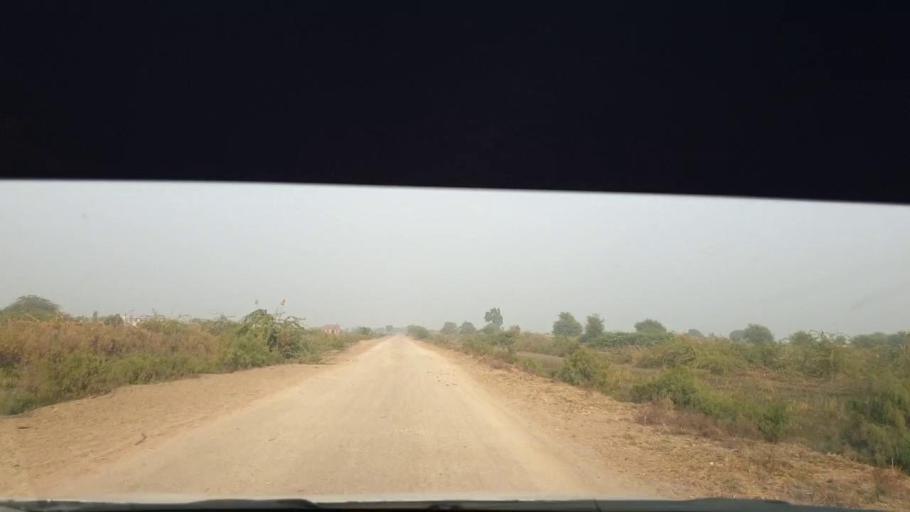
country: PK
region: Sindh
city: Berani
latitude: 25.8155
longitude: 68.8845
